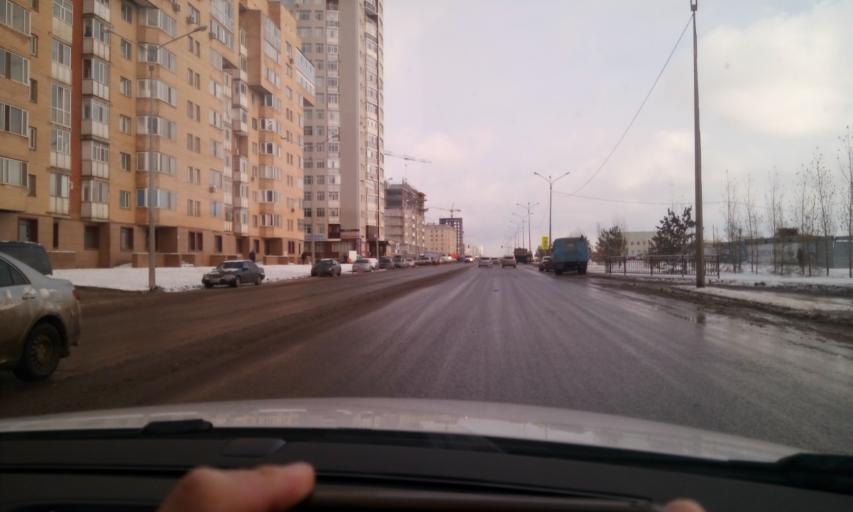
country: KZ
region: Astana Qalasy
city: Astana
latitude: 51.1235
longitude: 71.4768
